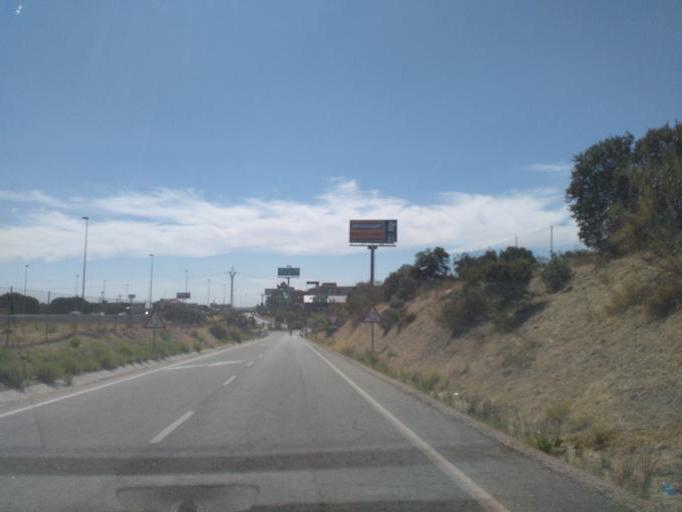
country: ES
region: Madrid
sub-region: Provincia de Madrid
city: Las Matas
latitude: 40.5592
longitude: -3.9020
